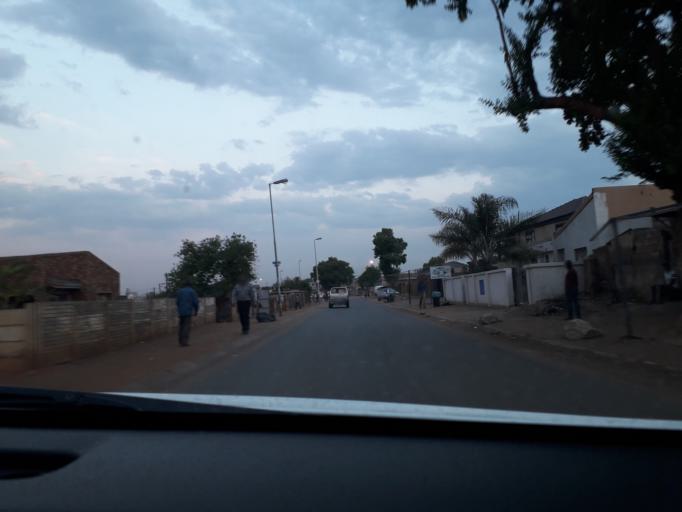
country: ZA
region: Gauteng
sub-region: Ekurhuleni Metropolitan Municipality
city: Tembisa
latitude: -25.9936
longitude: 28.2069
